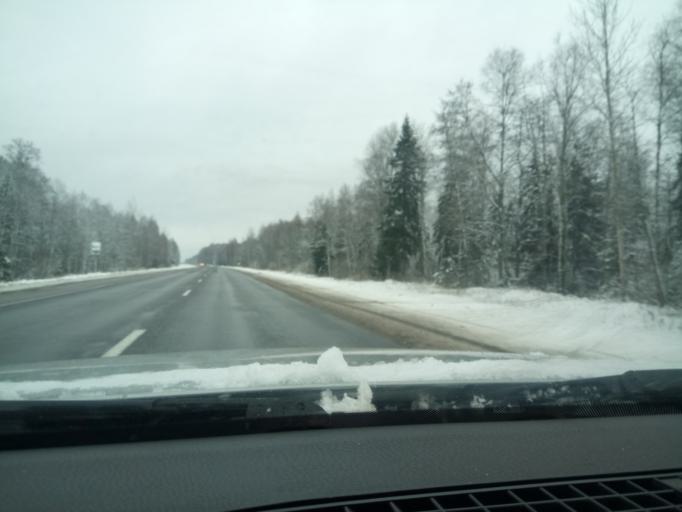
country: BY
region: Vitebsk
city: Vitebsk
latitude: 54.9577
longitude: 30.3571
